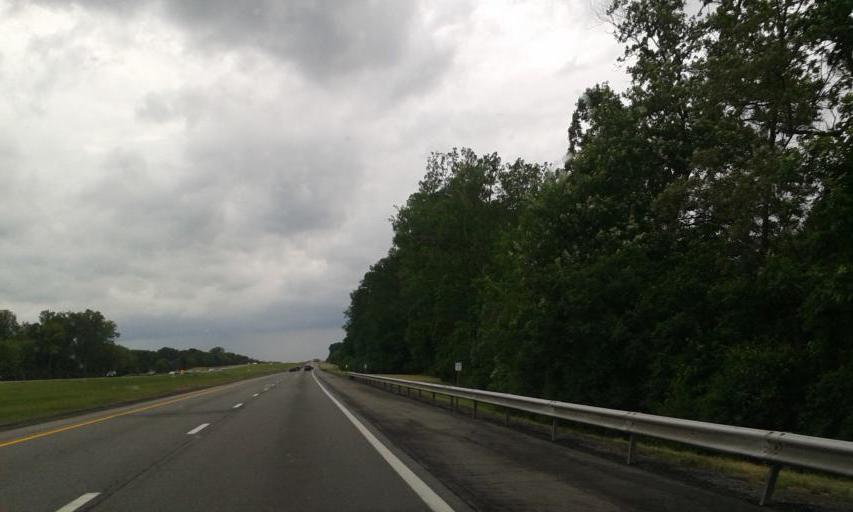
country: US
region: New York
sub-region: Ontario County
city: Clifton Springs
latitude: 42.9733
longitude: -77.1524
